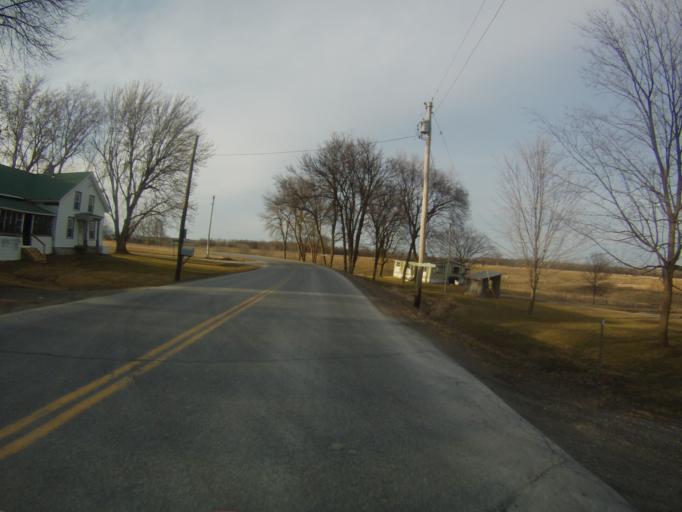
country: US
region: New York
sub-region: Essex County
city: Port Henry
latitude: 44.0546
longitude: -73.3761
